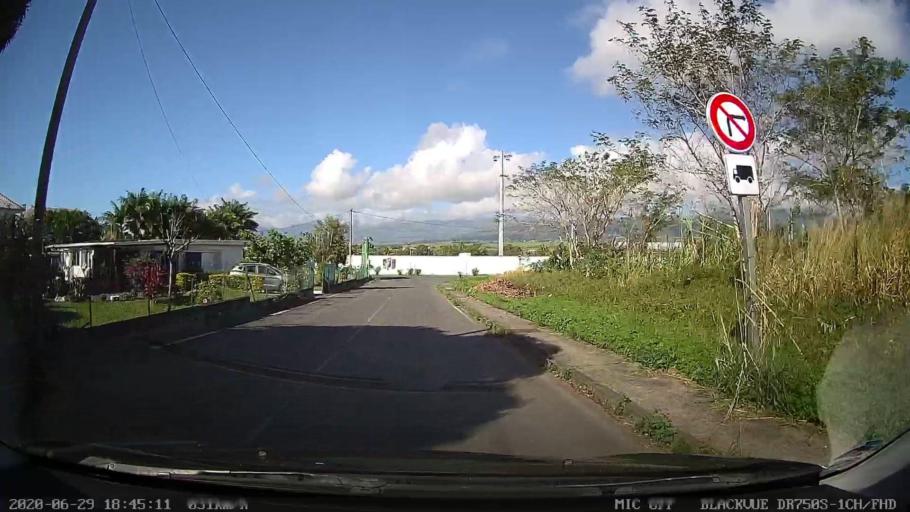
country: RE
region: Reunion
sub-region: Reunion
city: Bras-Panon
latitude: -20.9988
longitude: 55.6854
